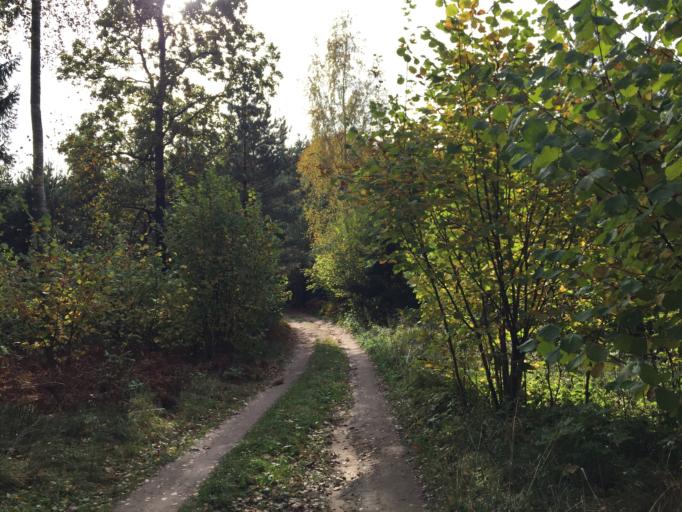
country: LV
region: Jaunpils
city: Jaunpils
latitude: 56.5963
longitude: 23.0142
